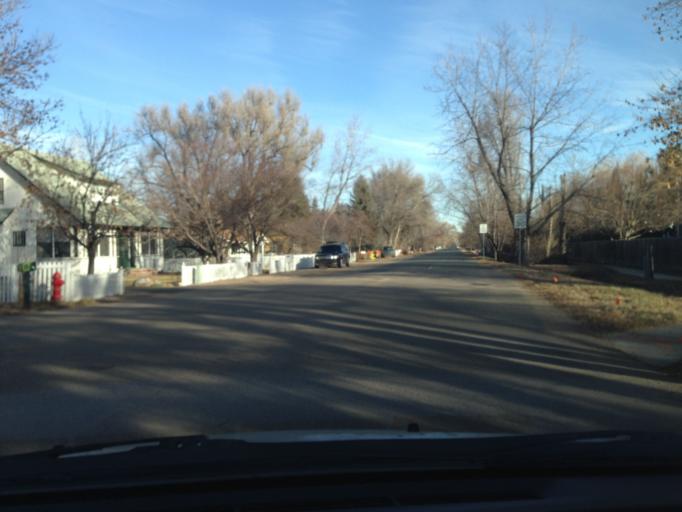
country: US
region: Colorado
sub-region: Boulder County
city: Niwot
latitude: 40.1052
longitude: -105.1694
